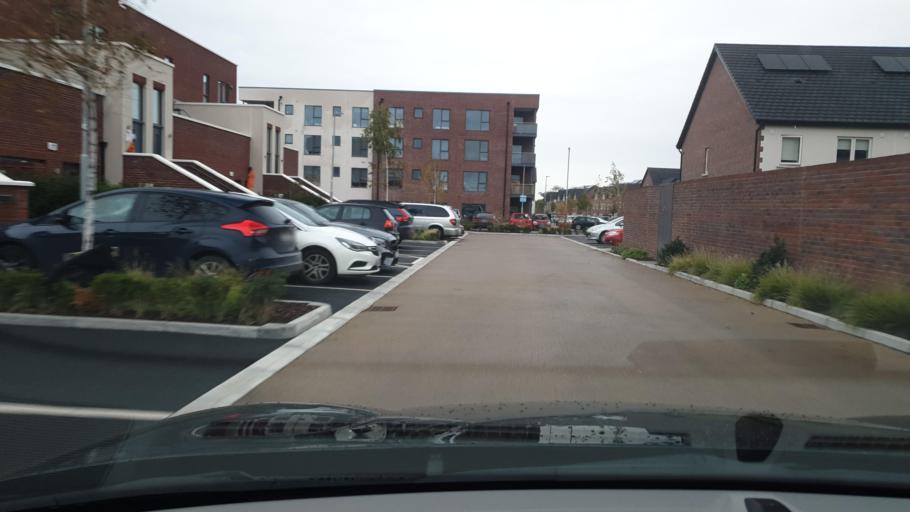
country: IE
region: Leinster
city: Lucan
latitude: 53.3451
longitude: -6.4731
